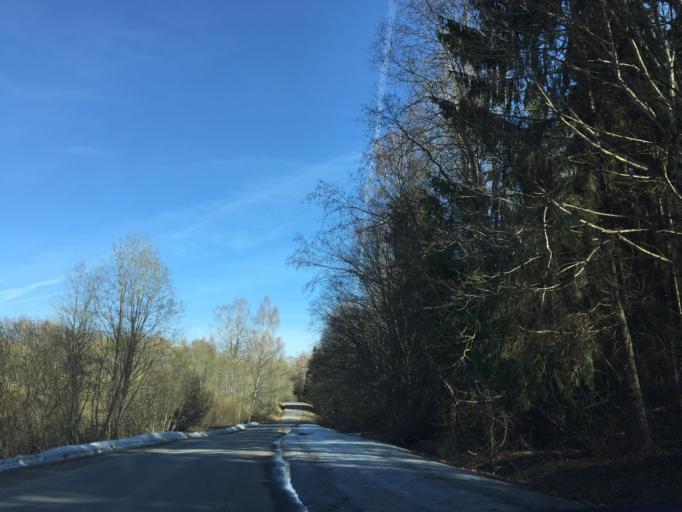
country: EE
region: Vorumaa
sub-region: Antsla vald
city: Vana-Antsla
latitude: 58.0177
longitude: 26.4543
